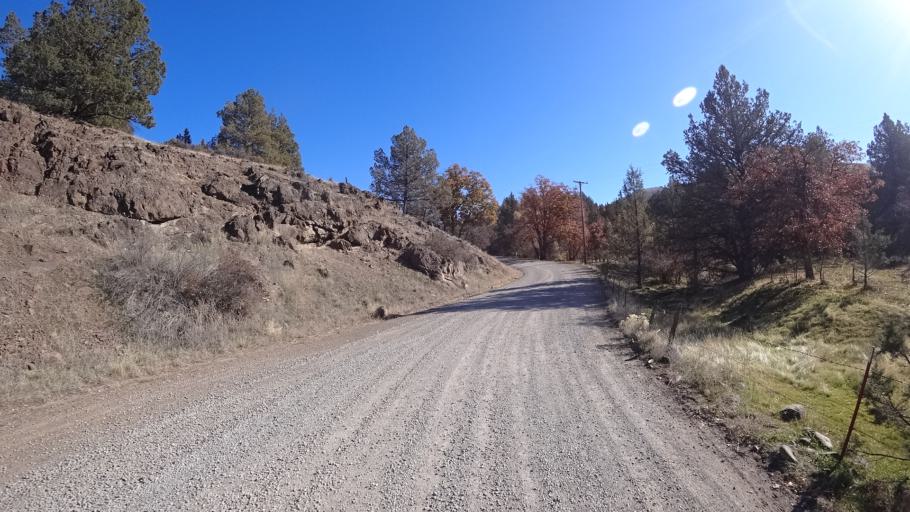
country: US
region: California
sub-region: Siskiyou County
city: Montague
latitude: 41.7926
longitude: -122.3529
